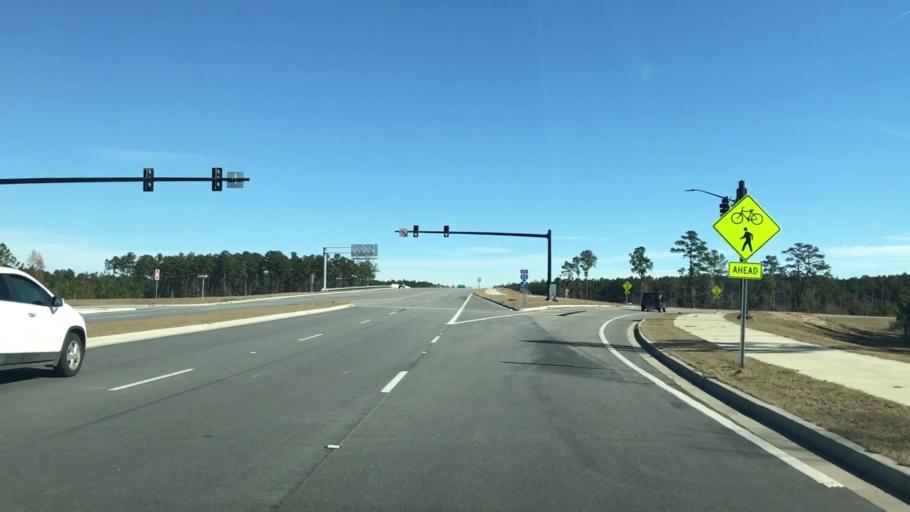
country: US
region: South Carolina
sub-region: Dorchester County
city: Summerville
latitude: 33.0514
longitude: -80.1670
